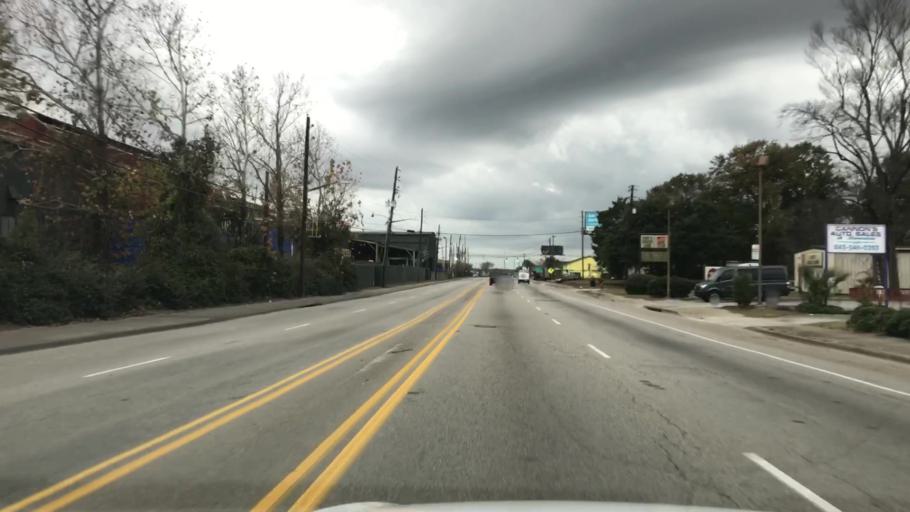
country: US
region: South Carolina
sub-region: Georgetown County
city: Georgetown
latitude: 33.3684
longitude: -79.2927
